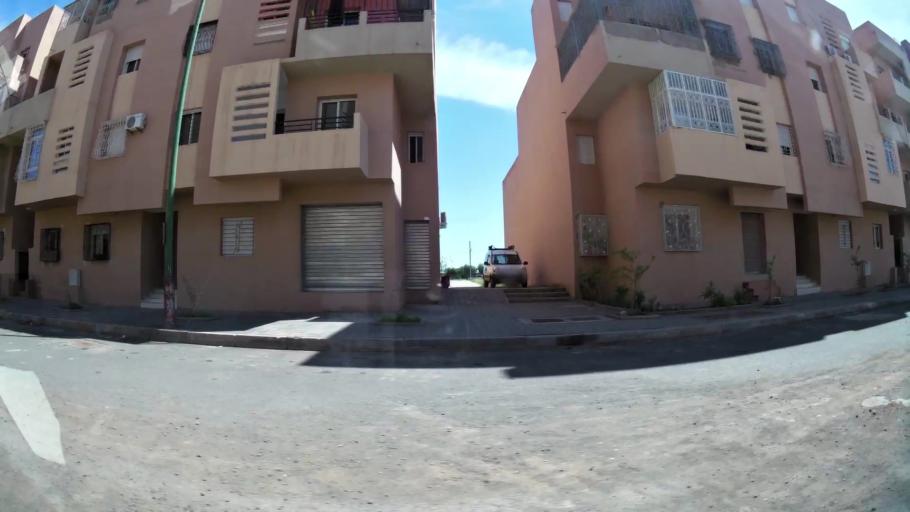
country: MA
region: Marrakech-Tensift-Al Haouz
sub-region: Marrakech
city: Marrakesh
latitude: 31.6288
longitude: -8.0741
